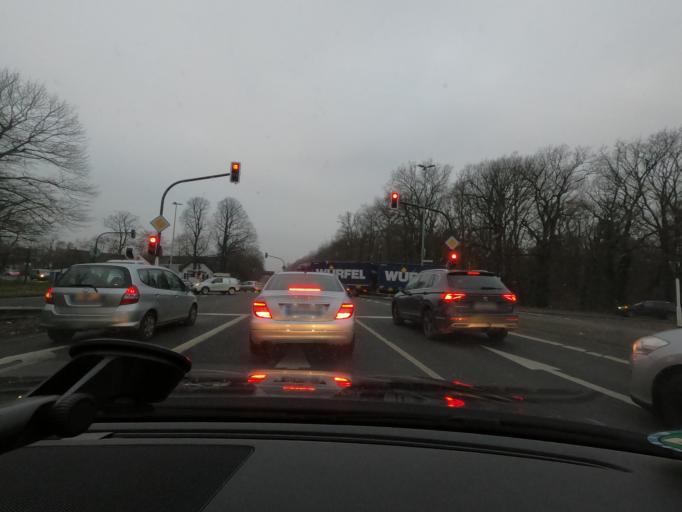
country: DE
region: North Rhine-Westphalia
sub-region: Regierungsbezirk Dusseldorf
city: Willich
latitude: 51.2995
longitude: 6.5312
